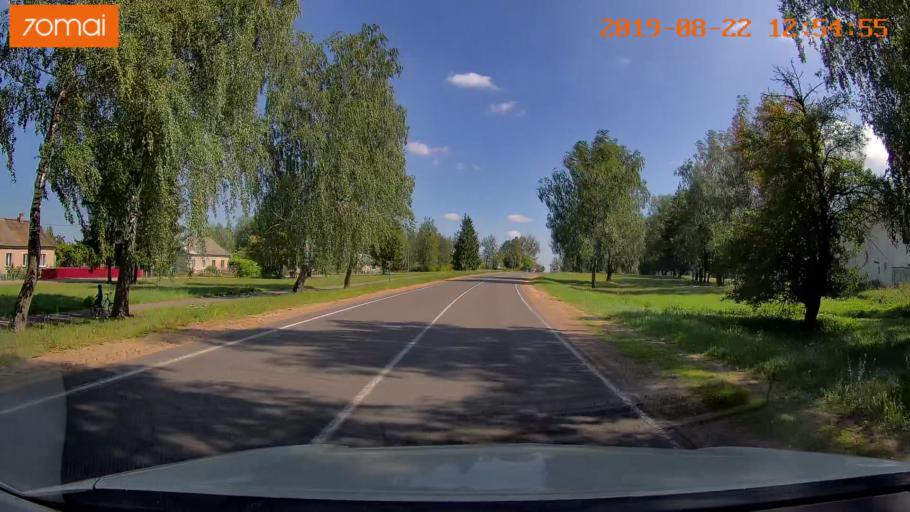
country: BY
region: Minsk
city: Prawdzinski
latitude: 53.4385
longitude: 27.7032
